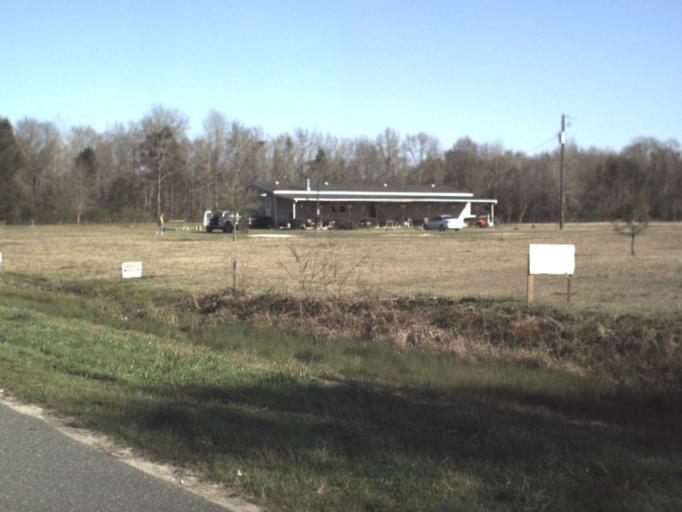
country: US
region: Florida
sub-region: Washington County
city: Chipley
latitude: 30.7882
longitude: -85.4266
